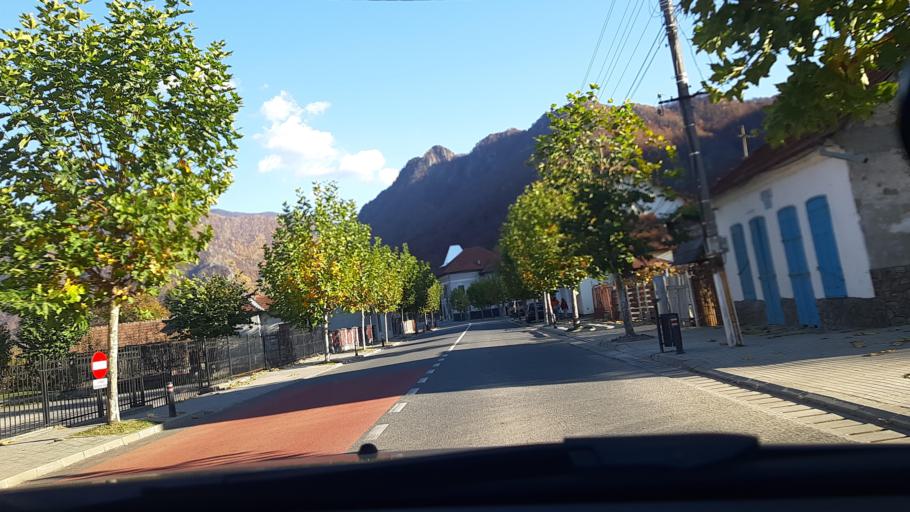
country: RO
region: Valcea
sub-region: Comuna Brezoi
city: Brezoi
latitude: 45.3368
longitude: 24.2498
